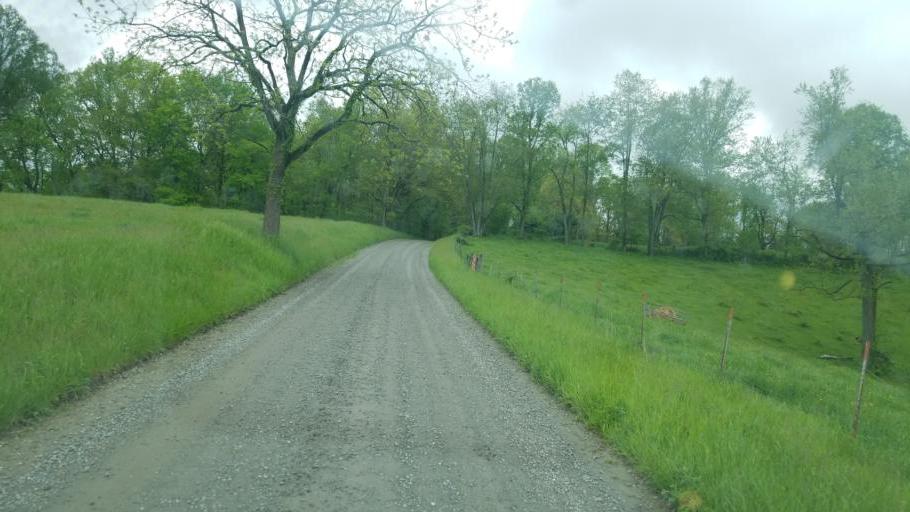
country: US
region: Ohio
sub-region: Harrison County
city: Cadiz
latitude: 40.3732
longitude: -81.1492
